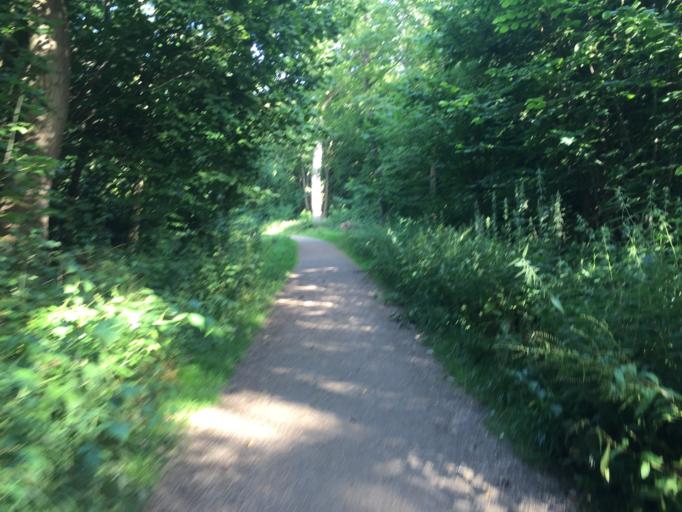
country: DK
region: South Denmark
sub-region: Odense Kommune
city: Neder Holluf
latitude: 55.3806
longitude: 10.4677
